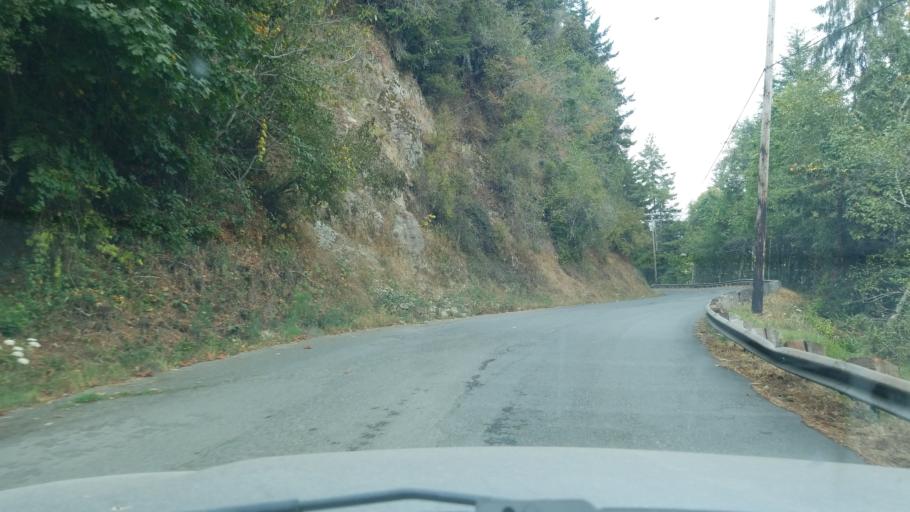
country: US
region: California
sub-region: Del Norte County
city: Bertsch-Oceanview
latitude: 41.5141
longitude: -124.0380
